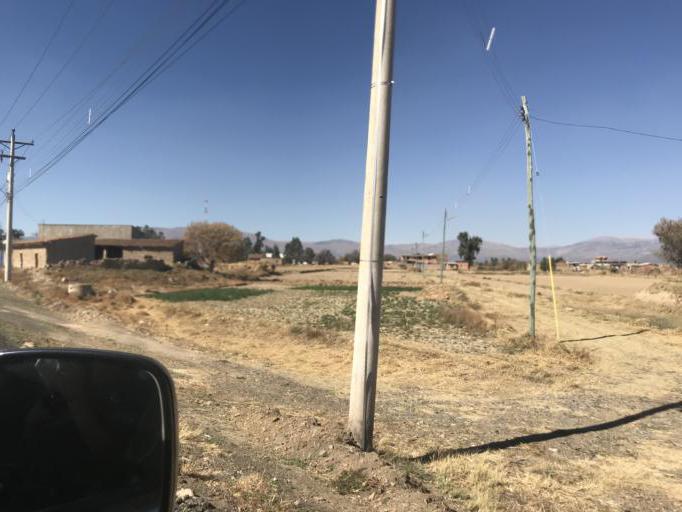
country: BO
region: Cochabamba
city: Cliza
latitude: -17.5678
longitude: -65.8927
